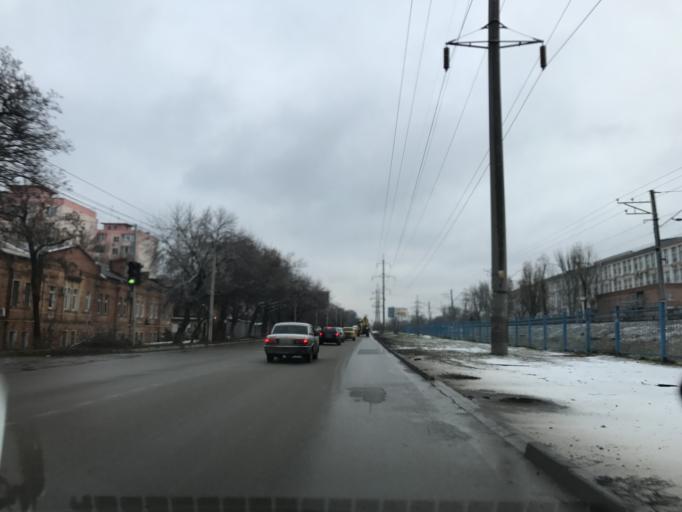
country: RU
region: Rostov
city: Rostov-na-Donu
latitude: 47.2449
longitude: 39.7076
